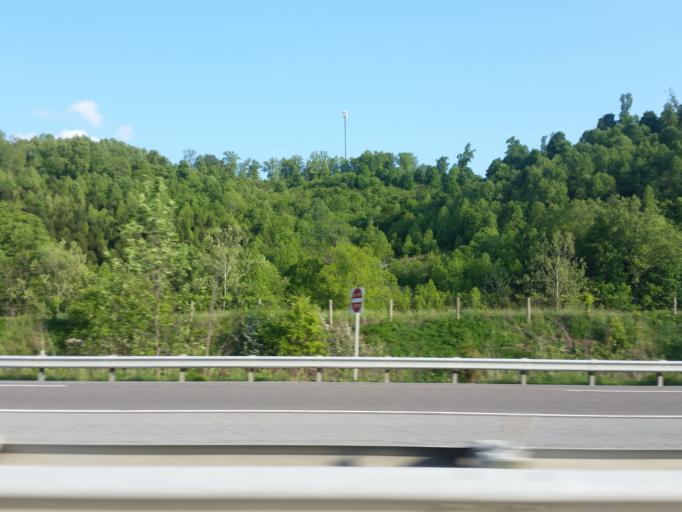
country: US
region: Virginia
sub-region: Russell County
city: Lebanon
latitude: 36.9148
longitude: -82.0102
